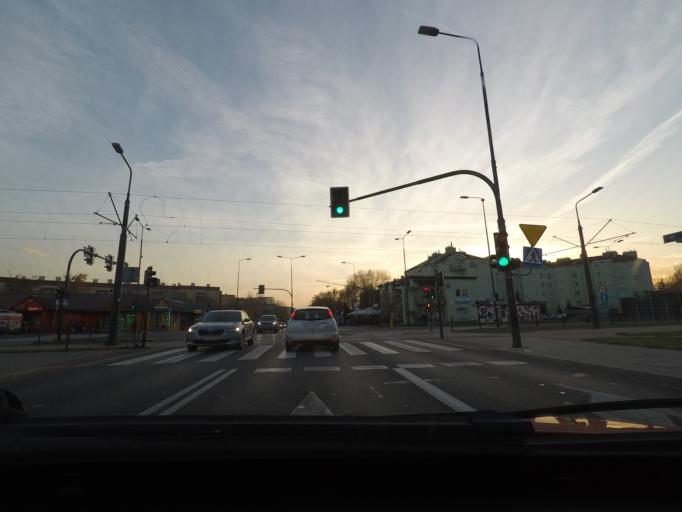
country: PL
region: Lesser Poland Voivodeship
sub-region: Krakow
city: Krakow
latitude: 50.0319
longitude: 19.9207
